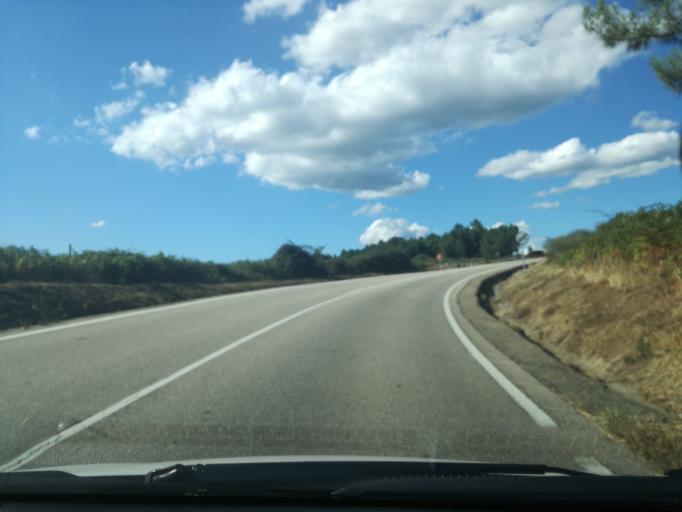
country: ES
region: Galicia
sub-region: Provincia de Ourense
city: Lobios
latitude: 41.8799
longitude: -8.0992
